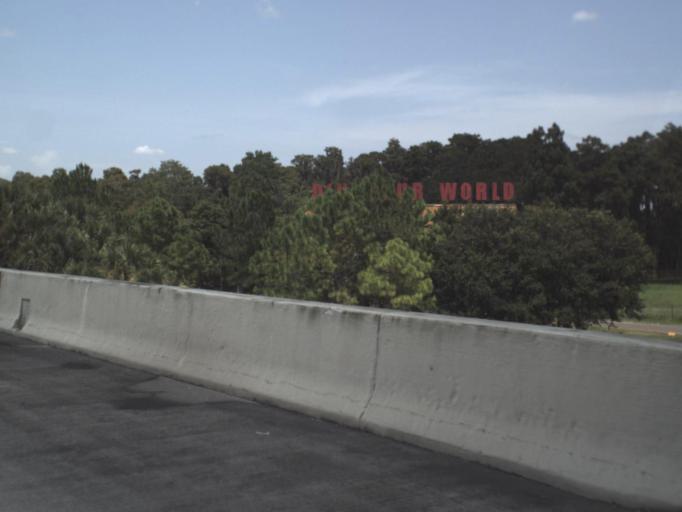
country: US
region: Florida
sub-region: Hillsborough County
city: Dover
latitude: 28.0272
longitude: -82.1869
